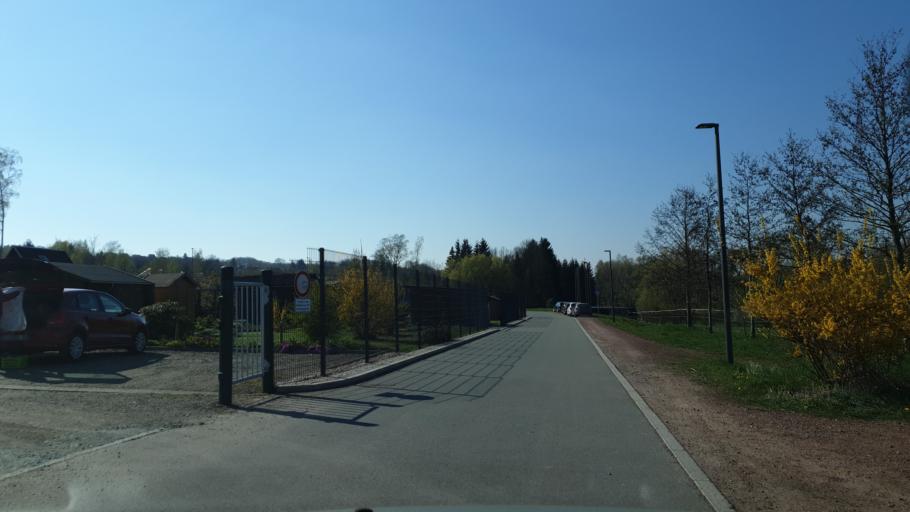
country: DE
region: Saxony
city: Oelsnitz
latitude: 50.7335
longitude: 12.6990
